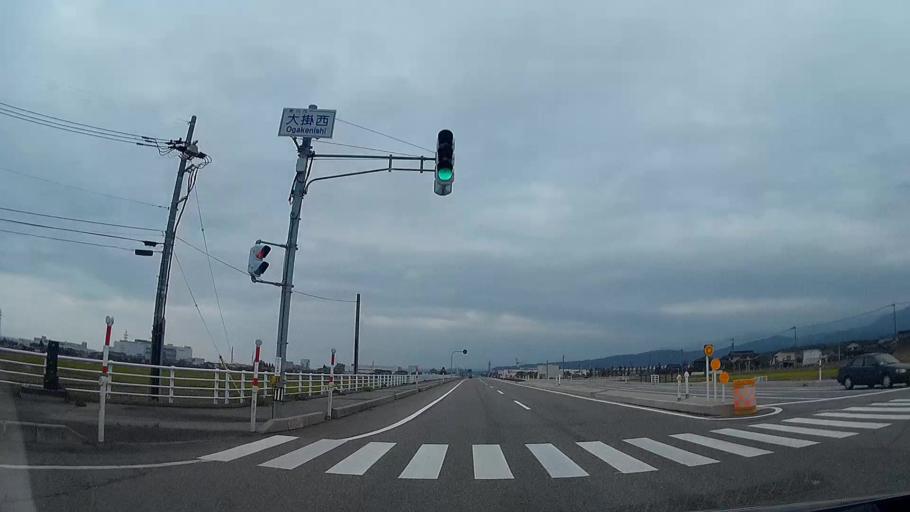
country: JP
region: Toyama
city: Uozu
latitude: 36.7734
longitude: 137.3869
